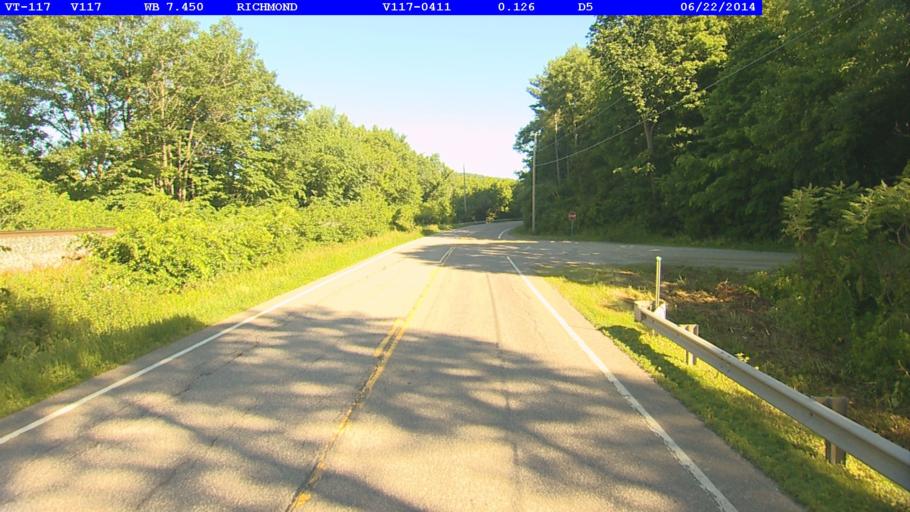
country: US
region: Vermont
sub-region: Chittenden County
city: Williston
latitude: 44.4326
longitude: -73.0200
